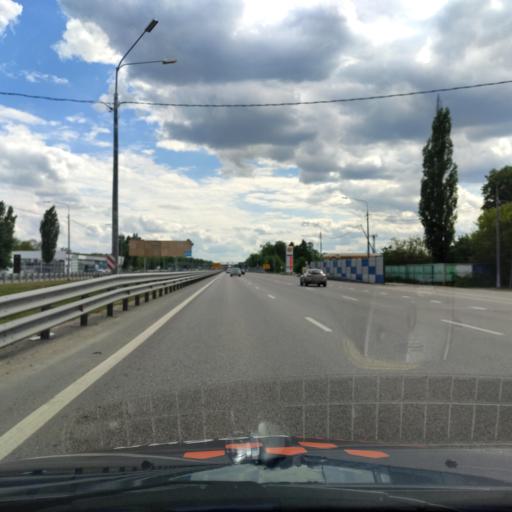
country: RU
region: Voronezj
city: Podgornoye
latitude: 51.7770
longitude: 39.1946
